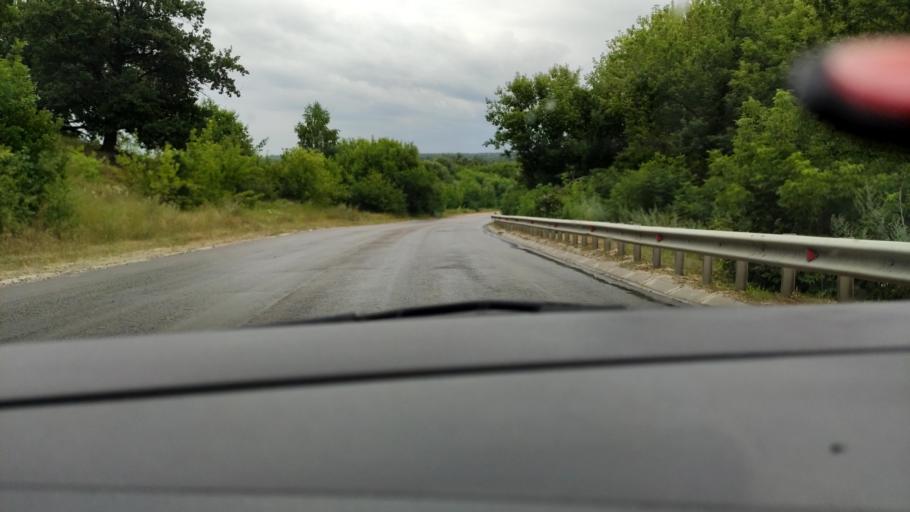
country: RU
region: Voronezj
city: Ramon'
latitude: 51.9042
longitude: 39.3390
